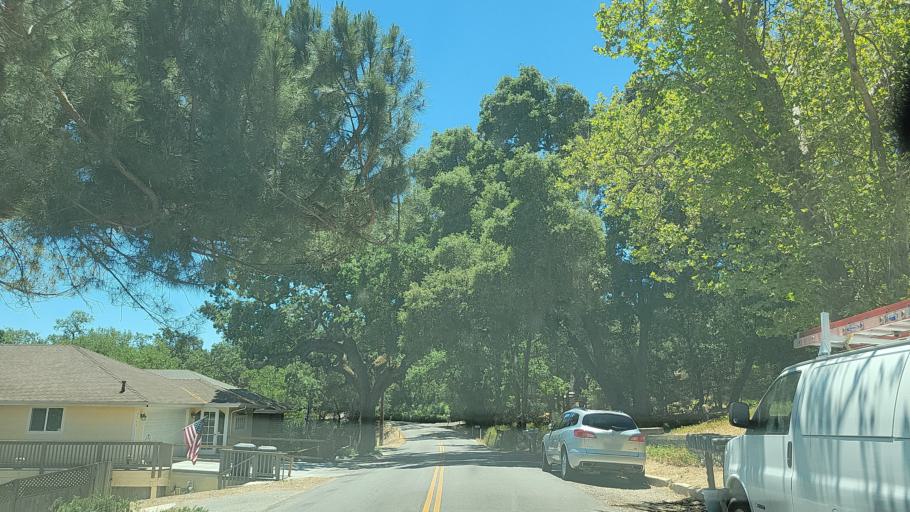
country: US
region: California
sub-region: San Luis Obispo County
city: Atascadero
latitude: 35.4968
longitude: -120.6709
